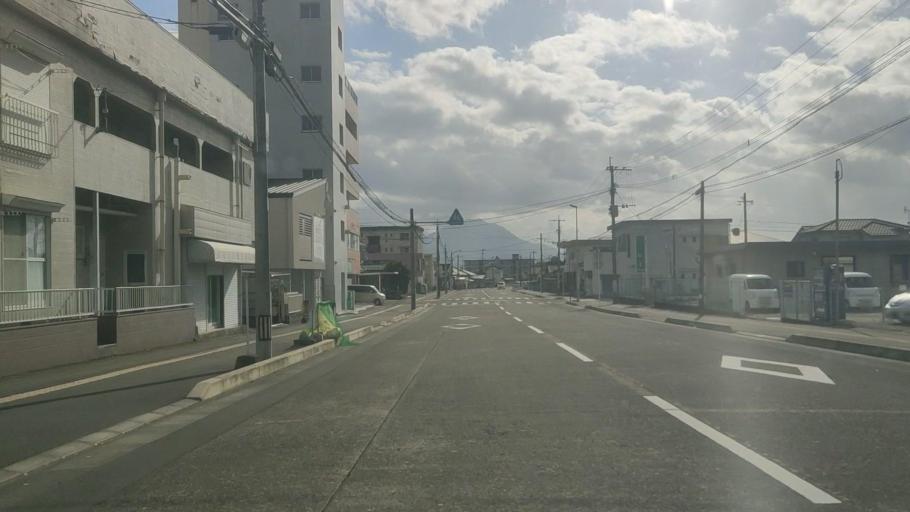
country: JP
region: Kagoshima
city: Kajiki
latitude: 31.7372
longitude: 130.6703
